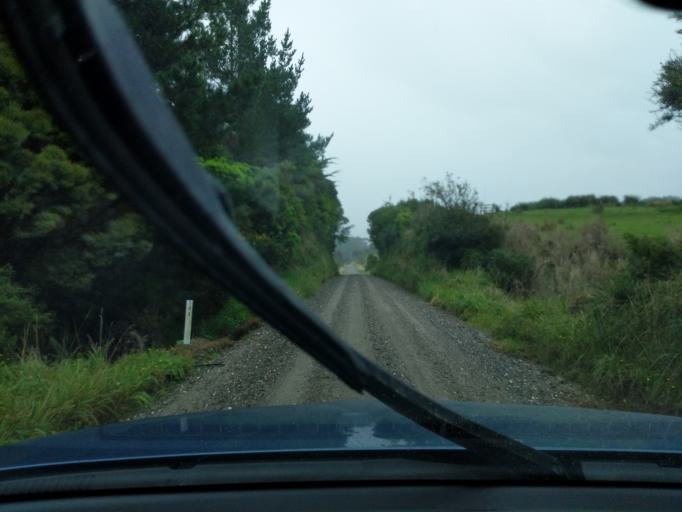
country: NZ
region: Tasman
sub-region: Tasman District
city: Takaka
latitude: -40.6330
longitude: 172.4902
